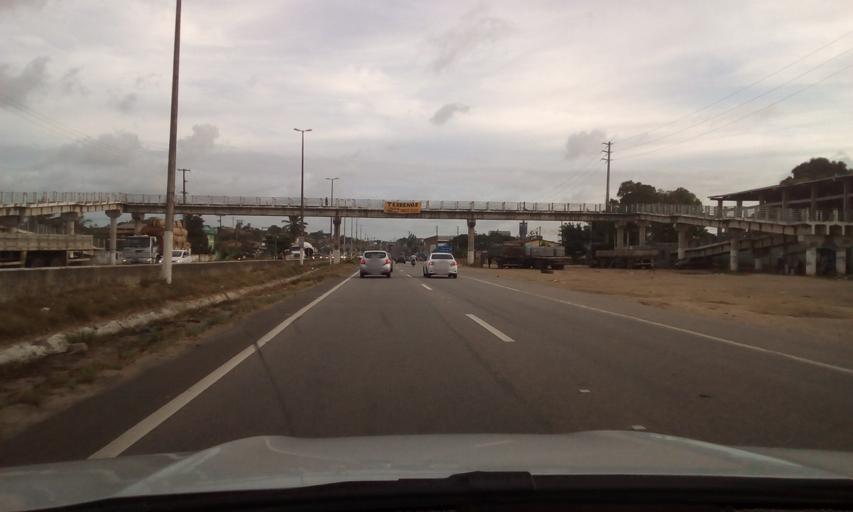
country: BR
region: Pernambuco
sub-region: Igarassu
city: Igarassu
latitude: -7.8268
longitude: -34.9152
